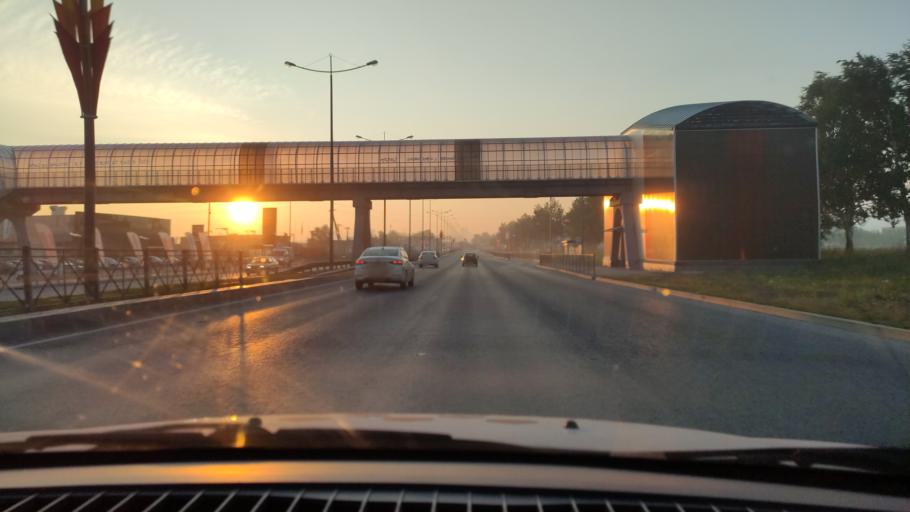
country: RU
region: Perm
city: Kondratovo
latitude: 57.9490
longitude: 56.0987
